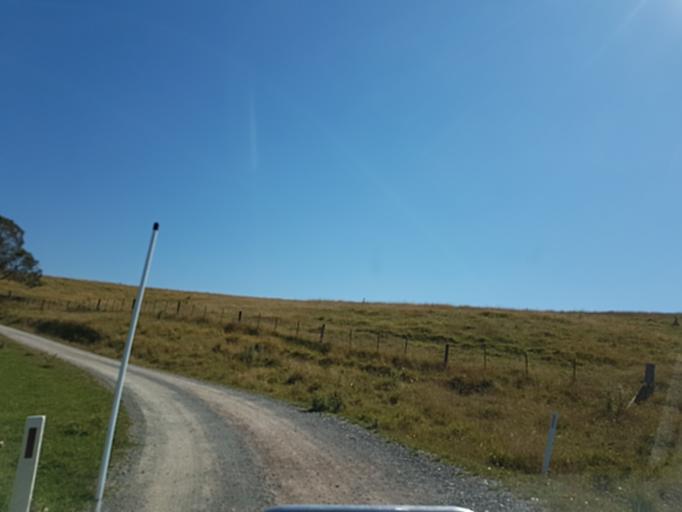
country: AU
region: Victoria
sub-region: East Gippsland
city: Lakes Entrance
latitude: -37.2345
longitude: 148.2697
